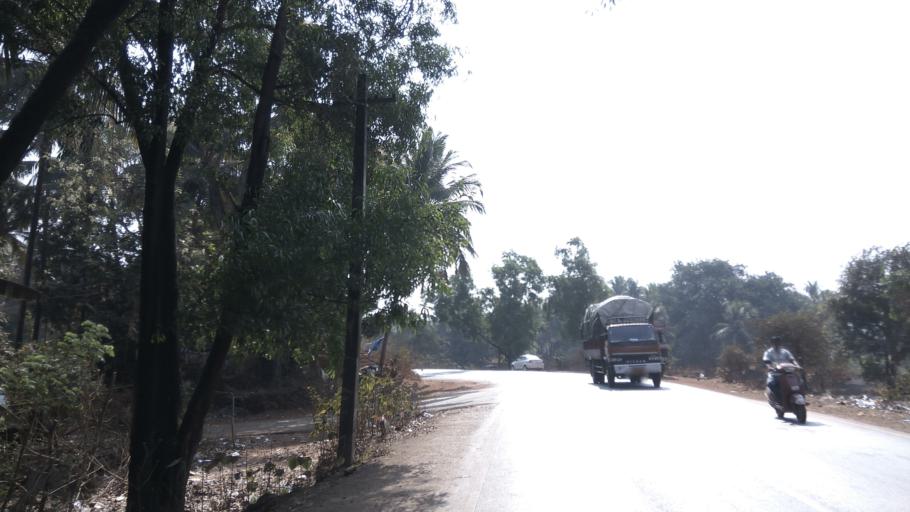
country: IN
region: Goa
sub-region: North Goa
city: Palle
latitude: 15.4133
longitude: 74.0806
